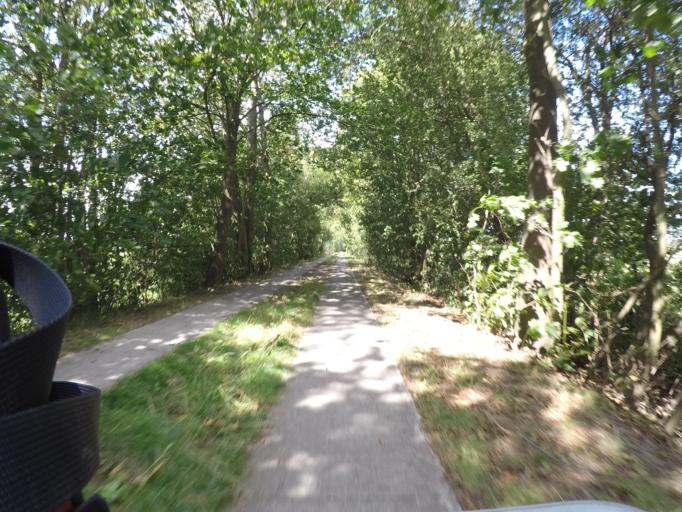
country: DE
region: Lower Saxony
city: Stelle
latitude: 53.4355
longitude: 10.1397
